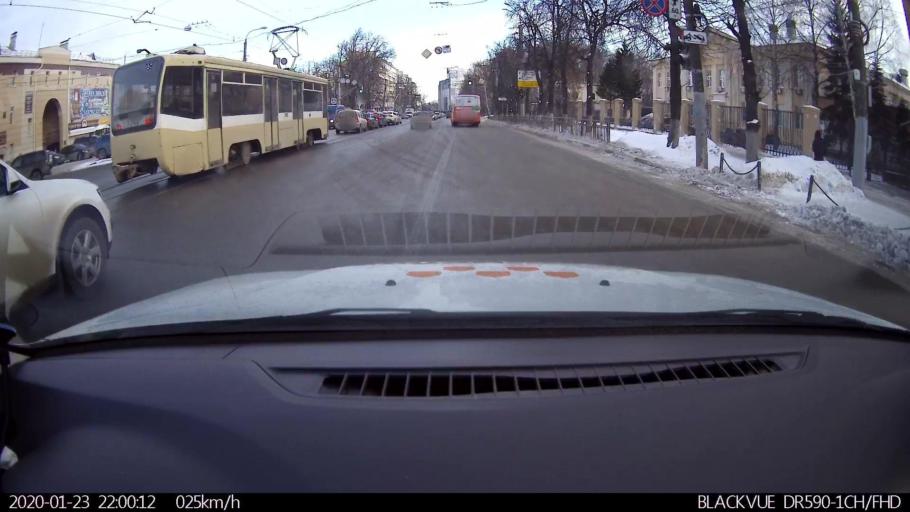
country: RU
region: Nizjnij Novgorod
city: Nizhniy Novgorod
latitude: 56.3068
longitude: 43.9922
